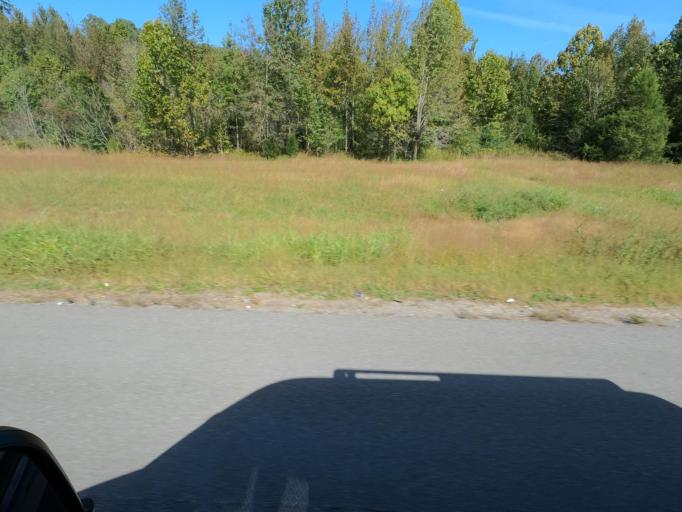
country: US
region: Tennessee
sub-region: Madison County
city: Three Way
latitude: 35.6707
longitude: -88.9380
